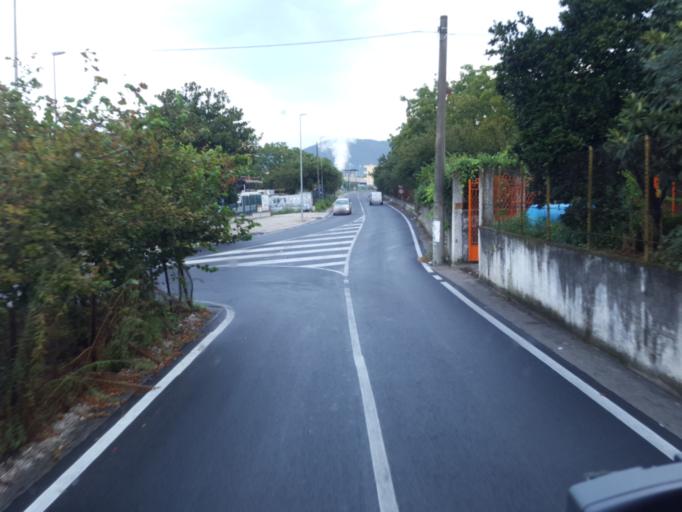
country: IT
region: Campania
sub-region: Provincia di Napoli
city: Palma Campania
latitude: 40.8773
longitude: 14.5617
